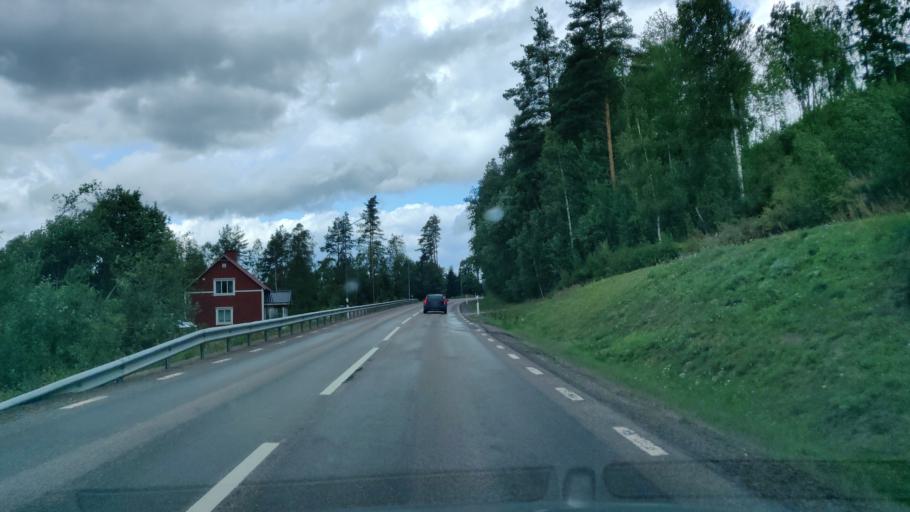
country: SE
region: Vaermland
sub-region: Torsby Kommun
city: Torsby
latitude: 60.5991
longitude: 13.0667
